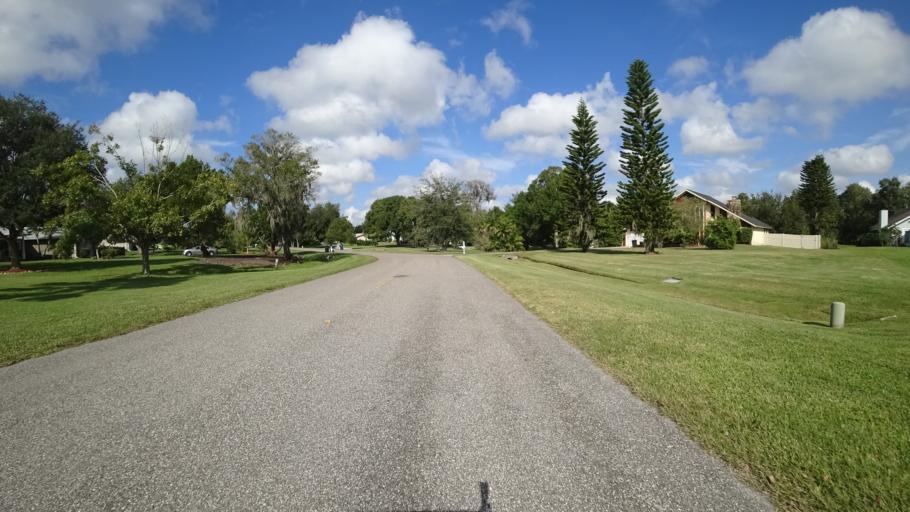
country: US
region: Florida
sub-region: Sarasota County
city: North Sarasota
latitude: 27.3986
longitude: -82.5157
